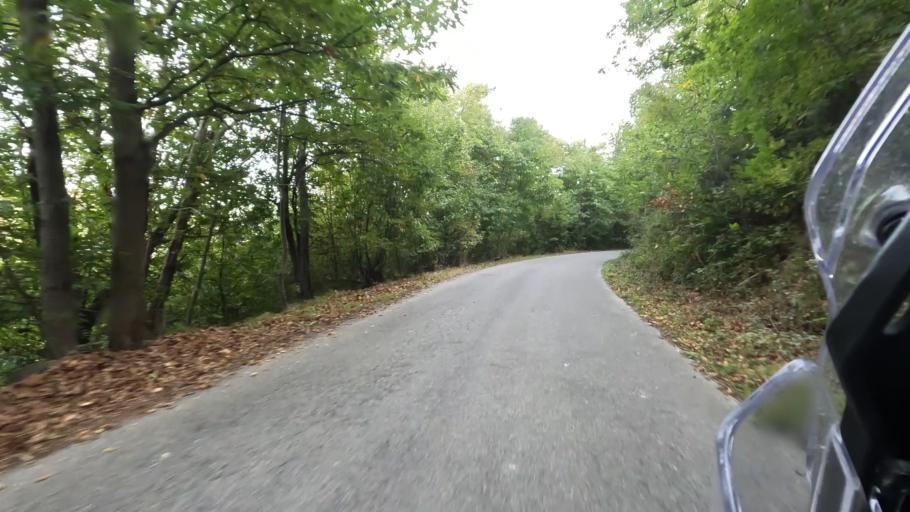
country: IT
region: Liguria
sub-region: Provincia di Savona
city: San Giovanni
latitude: 44.3936
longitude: 8.5373
